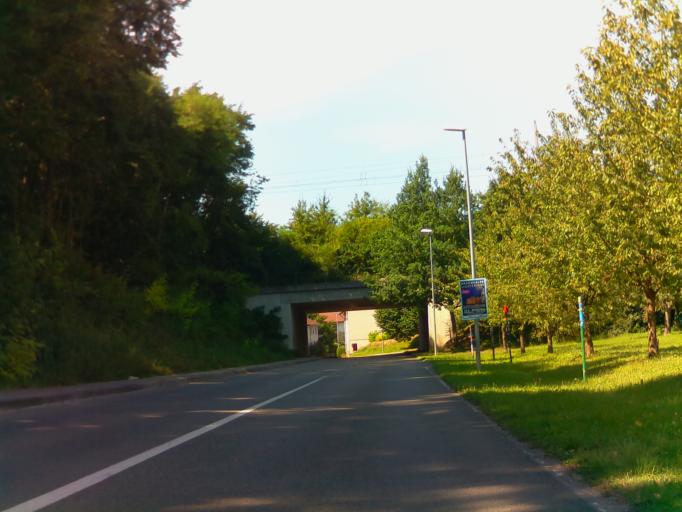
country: DE
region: Baden-Wuerttemberg
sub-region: Karlsruhe Region
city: Oberderdingen
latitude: 49.0830
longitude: 8.7789
